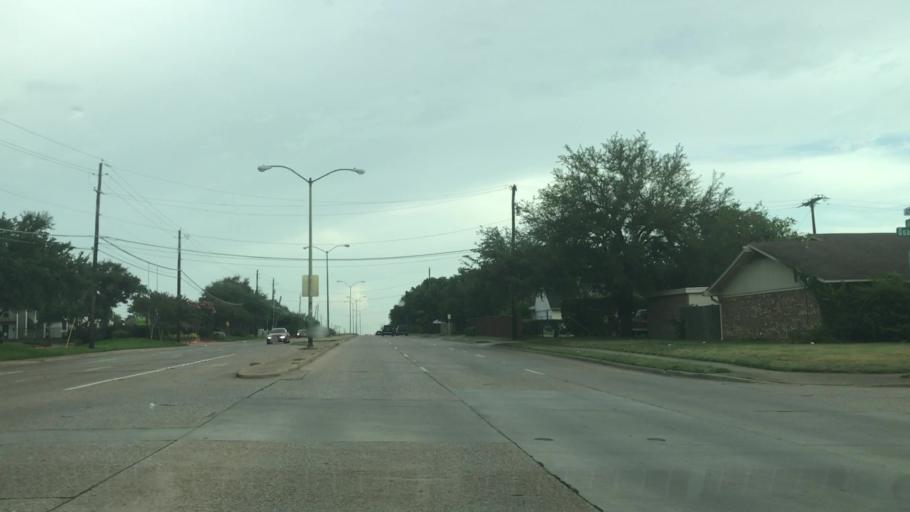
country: US
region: Texas
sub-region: Dallas County
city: Garland
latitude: 32.8696
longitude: -96.6832
